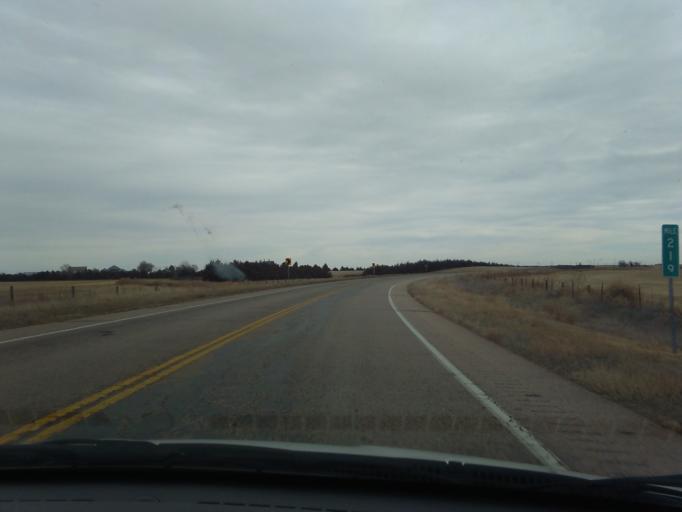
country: US
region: Colorado
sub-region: Yuma County
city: Yuma
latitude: 40.1471
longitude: -102.7822
